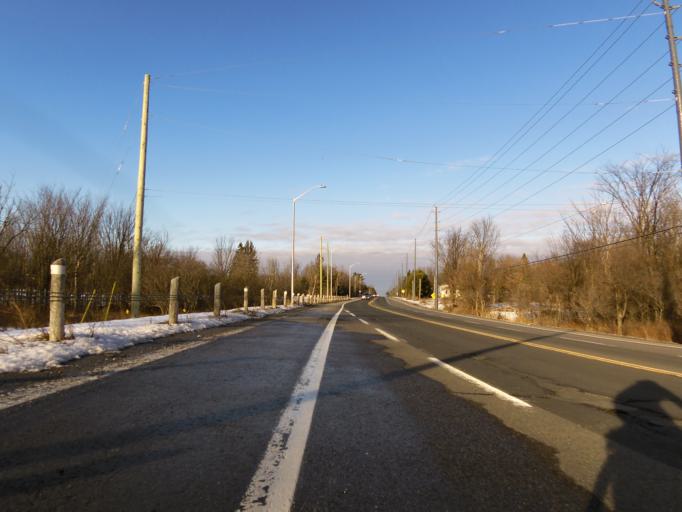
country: CA
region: Ontario
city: Bells Corners
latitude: 45.2837
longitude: -75.8382
